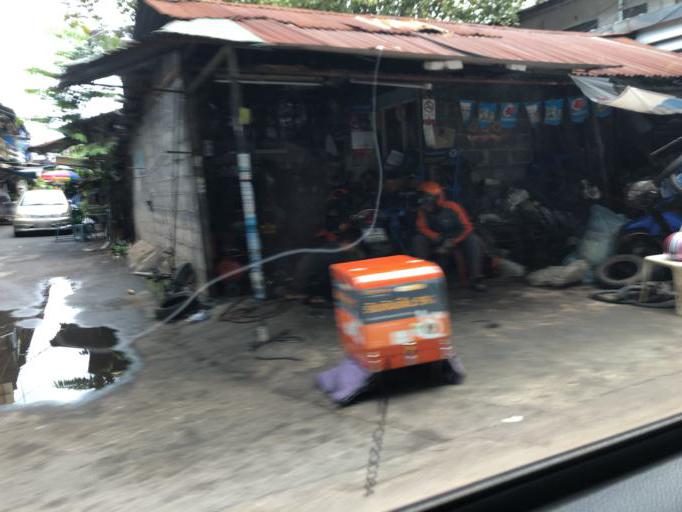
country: TH
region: Bangkok
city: Don Mueang
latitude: 13.9136
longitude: 100.5971
